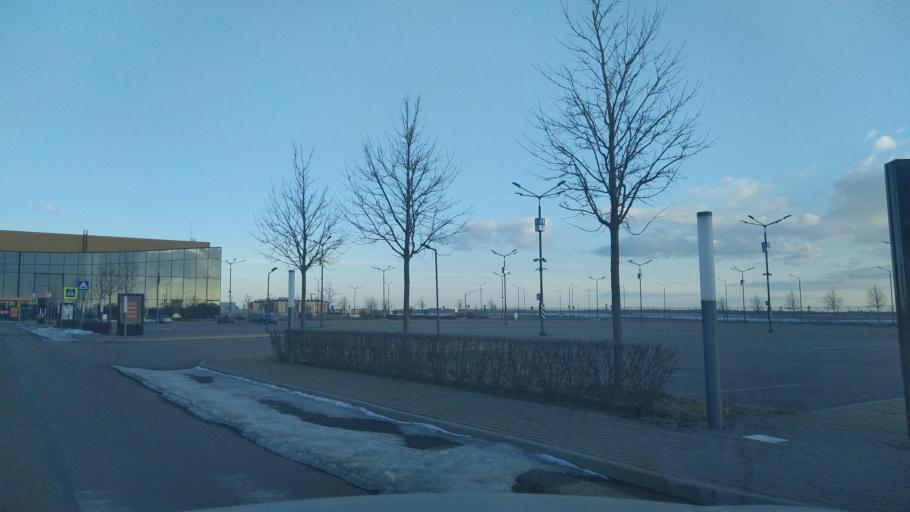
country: RU
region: St.-Petersburg
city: Aleksandrovskaya
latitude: 59.7609
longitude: 30.3497
